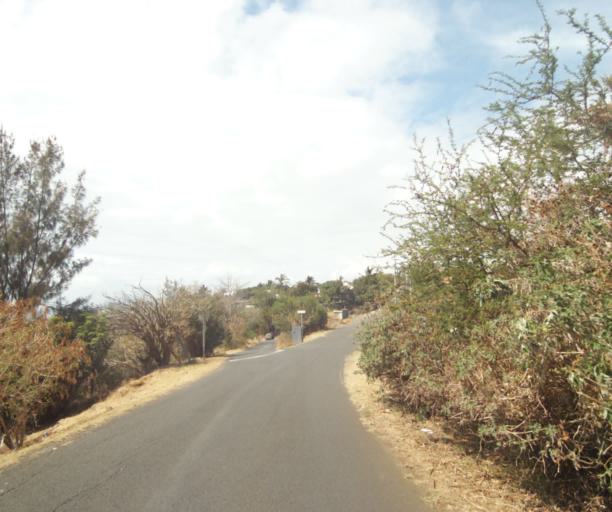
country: RE
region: Reunion
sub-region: Reunion
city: Saint-Paul
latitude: -21.0558
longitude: 55.2559
